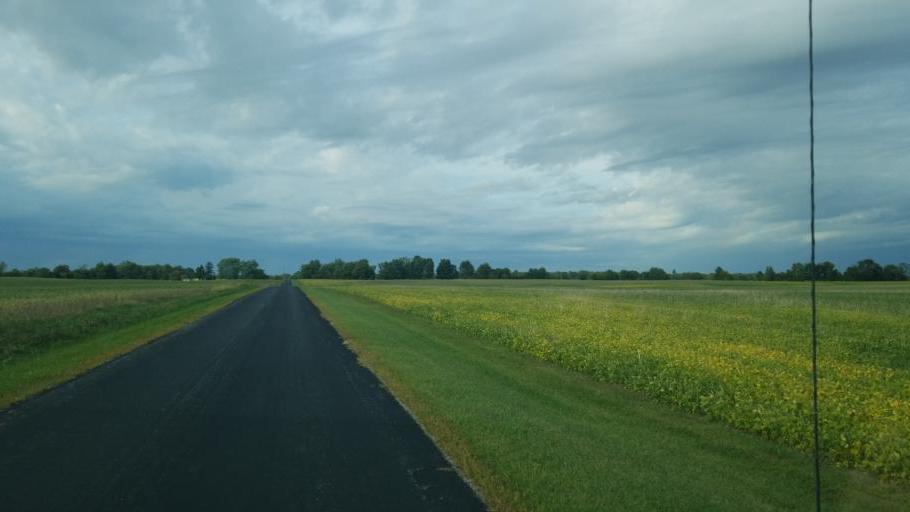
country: US
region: Ohio
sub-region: Wyandot County
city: Upper Sandusky
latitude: 40.9230
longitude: -83.1505
